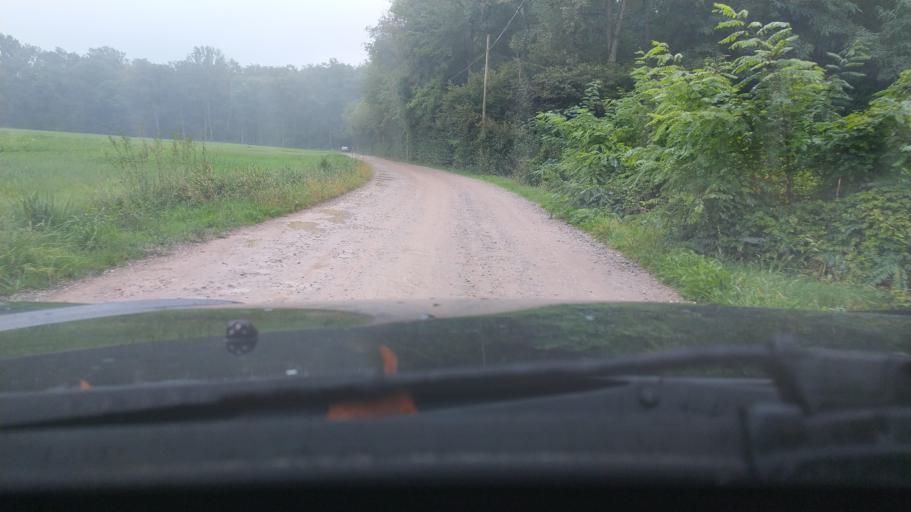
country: IT
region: Lombardy
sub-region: Provincia di Varese
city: Angera
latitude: 45.7640
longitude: 8.5876
